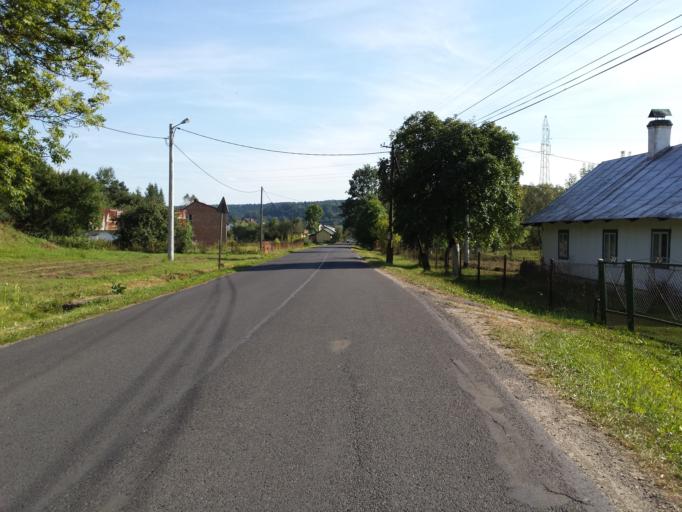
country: PL
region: Subcarpathian Voivodeship
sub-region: Powiat leski
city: Olszanica
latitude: 49.4847
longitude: 22.4435
